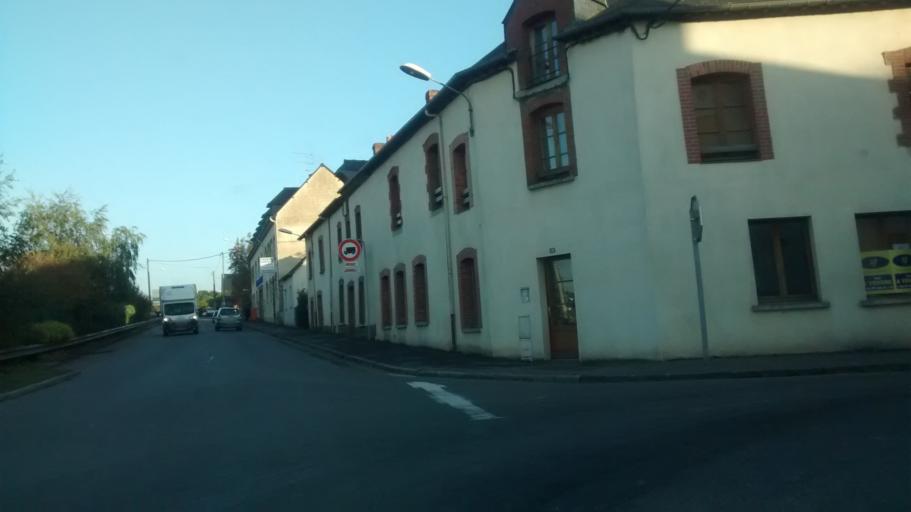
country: FR
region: Brittany
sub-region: Departement d'Ille-et-Vilaine
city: Le Rheu
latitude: 48.1228
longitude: -1.8205
